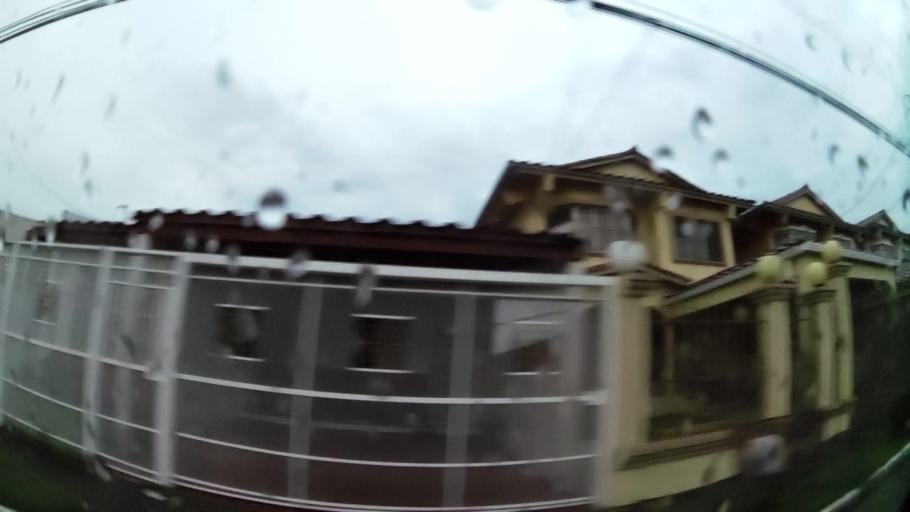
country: PA
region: Panama
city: Las Cumbres
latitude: 9.0447
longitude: -79.5234
